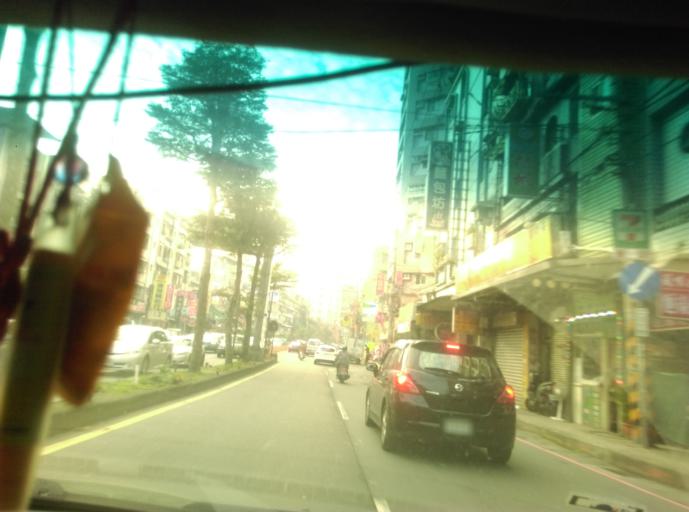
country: TW
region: Taiwan
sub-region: Keelung
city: Keelung
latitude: 25.1403
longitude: 121.7123
